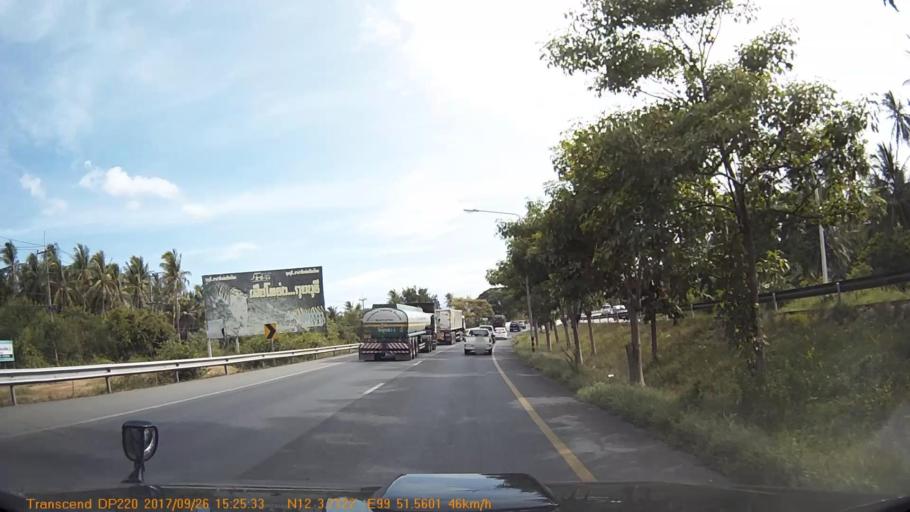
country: TH
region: Prachuap Khiri Khan
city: Kui Buri
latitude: 12.0618
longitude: 99.8593
